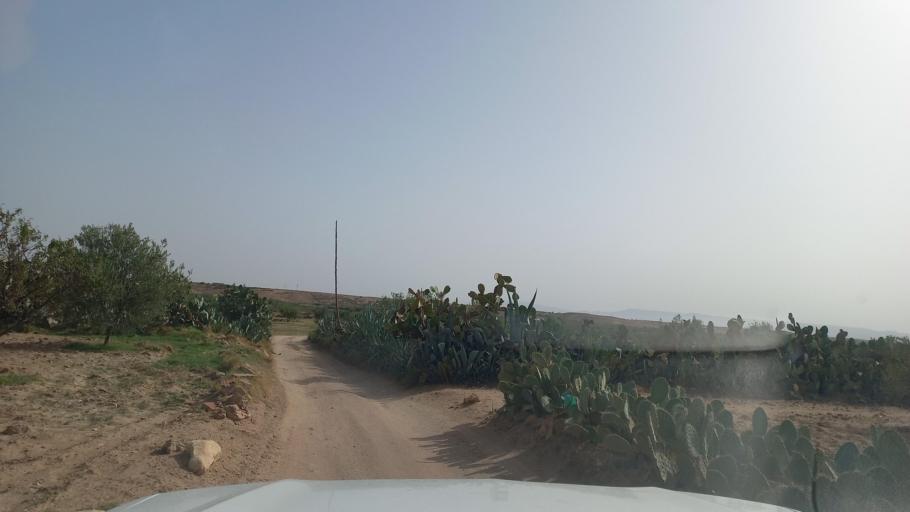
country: TN
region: Al Qasrayn
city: Kasserine
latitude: 35.2952
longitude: 8.9599
